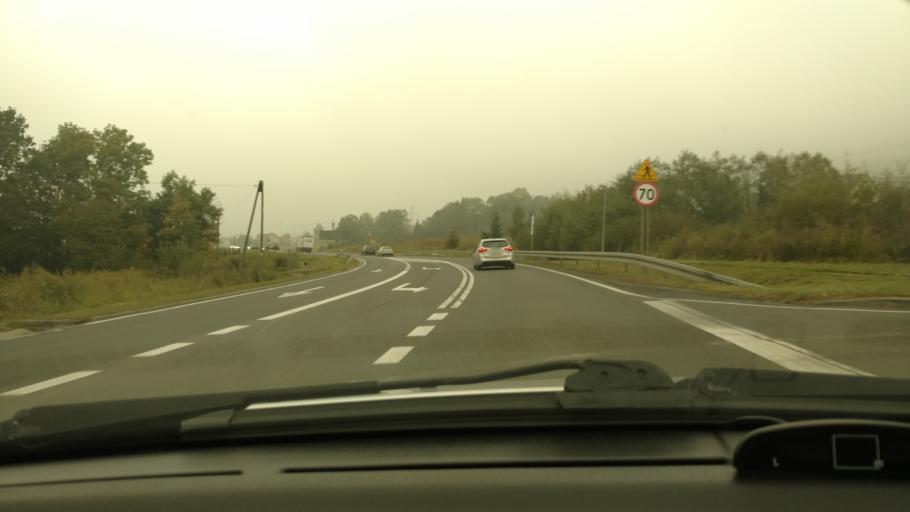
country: PL
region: Lesser Poland Voivodeship
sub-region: Powiat nowosadecki
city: Kamionka Wielka
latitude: 49.6168
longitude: 20.8669
